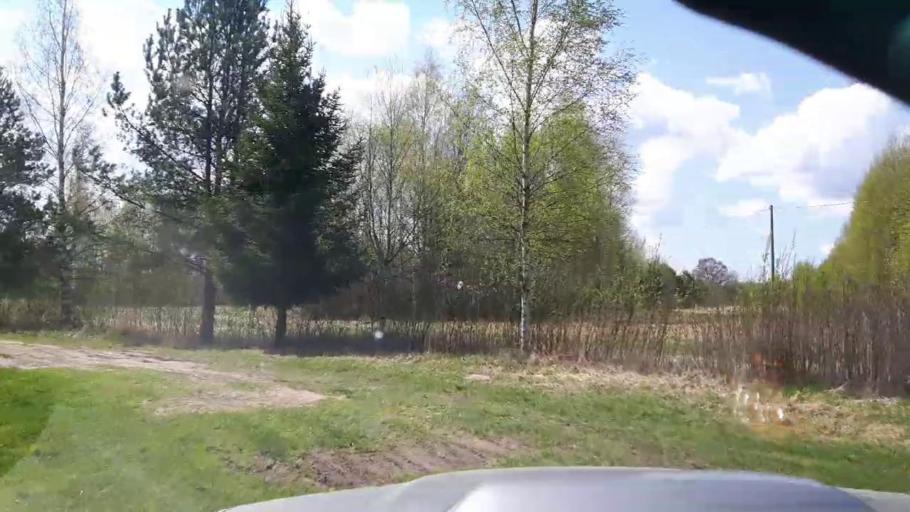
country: EE
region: Paernumaa
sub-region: Vaendra vald (alev)
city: Vandra
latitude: 58.4840
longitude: 25.0011
